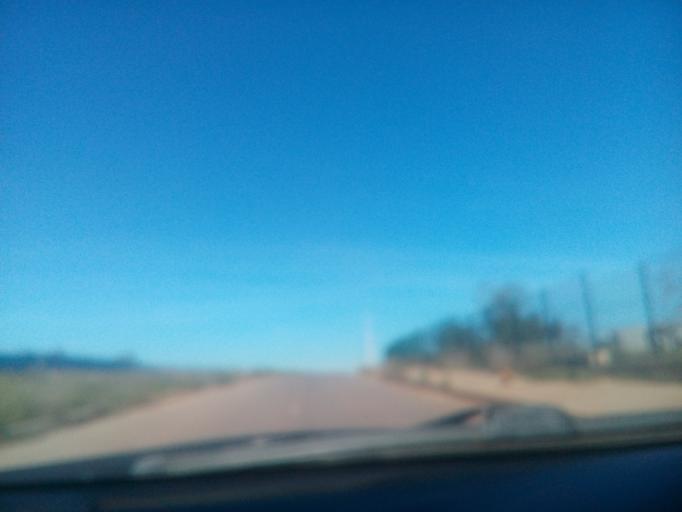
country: DZ
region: Oran
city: Bir el Djir
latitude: 35.7300
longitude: -0.5414
